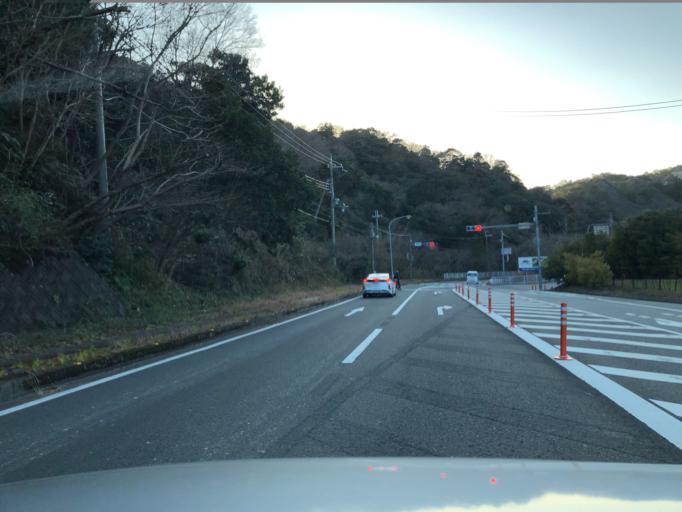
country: JP
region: Wakayama
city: Tanabe
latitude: 33.6628
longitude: 135.3727
